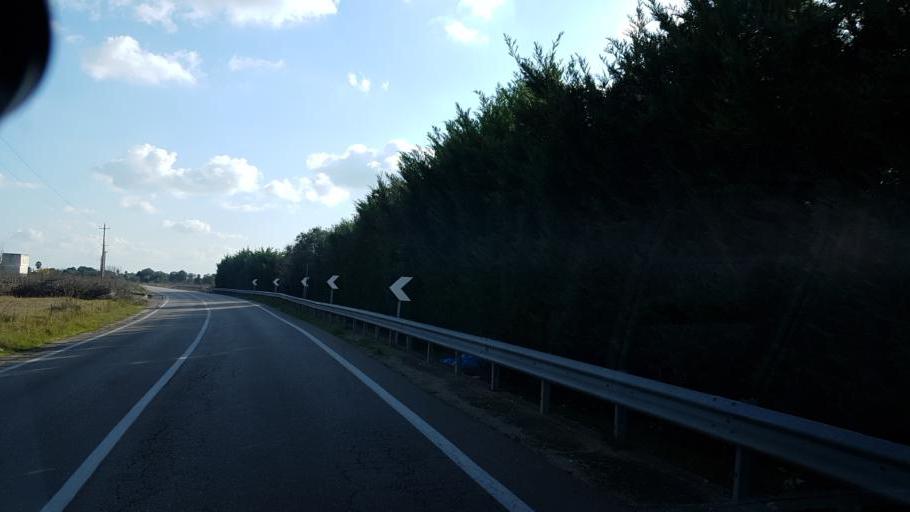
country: IT
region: Apulia
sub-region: Provincia di Lecce
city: Leverano
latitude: 40.3115
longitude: 17.9843
